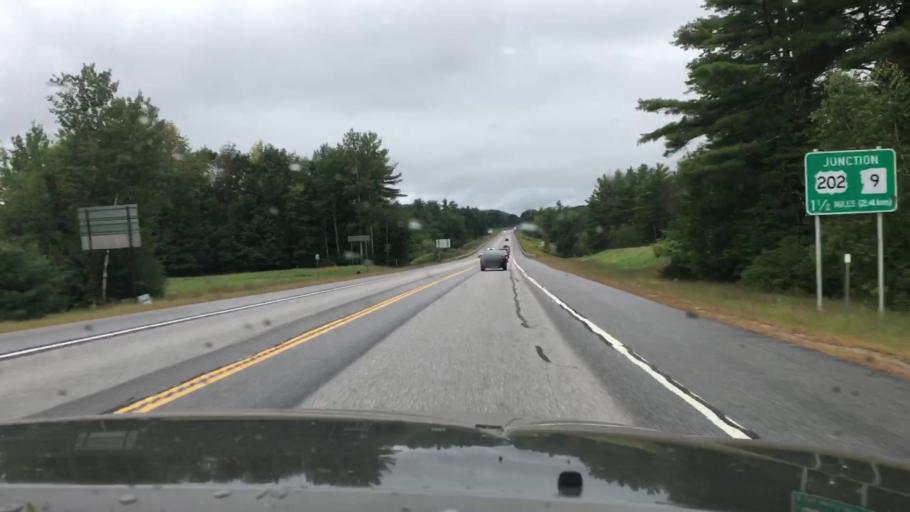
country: US
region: New Hampshire
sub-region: Hillsborough County
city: Hillsboro
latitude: 43.1298
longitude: -71.8865
